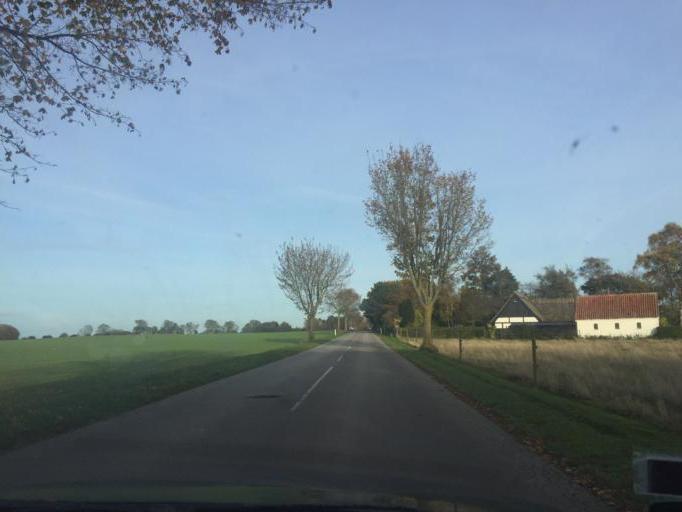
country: DK
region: Zealand
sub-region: Stevns Kommune
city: Store Heddinge
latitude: 55.2734
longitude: 12.4173
